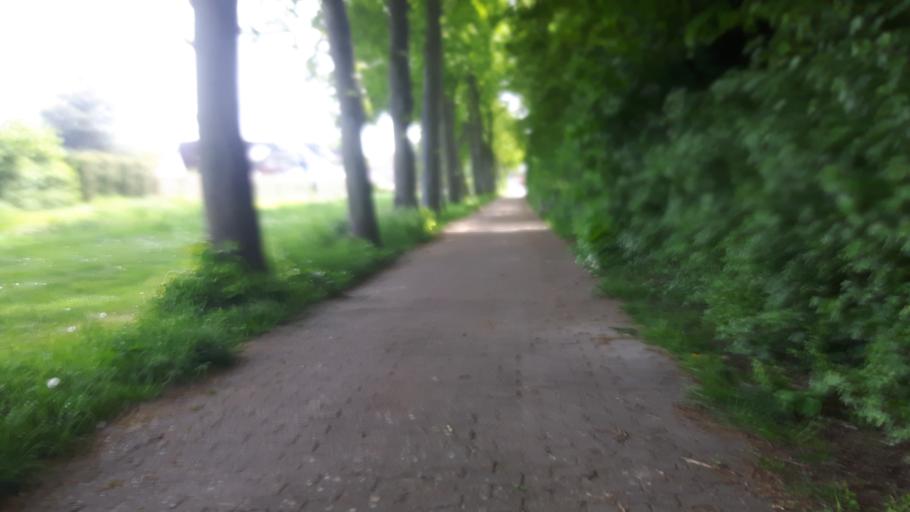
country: DE
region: Lower Saxony
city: Stuhr
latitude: 53.0626
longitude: 8.7612
